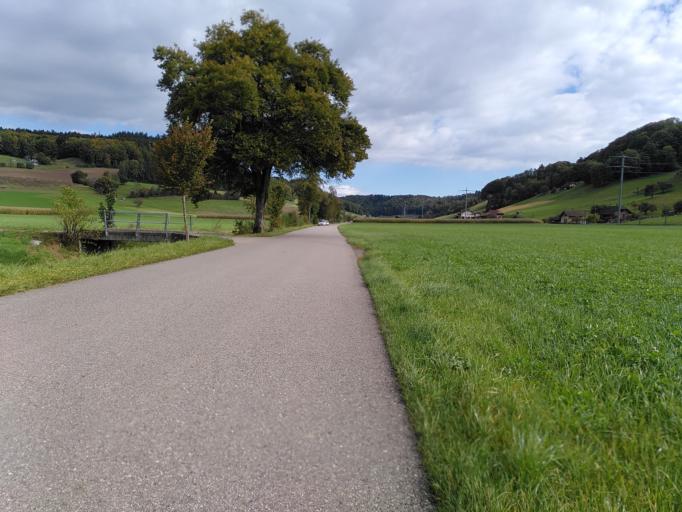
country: CH
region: Bern
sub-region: Oberaargau
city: Seeberg
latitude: 47.1290
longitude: 7.6769
